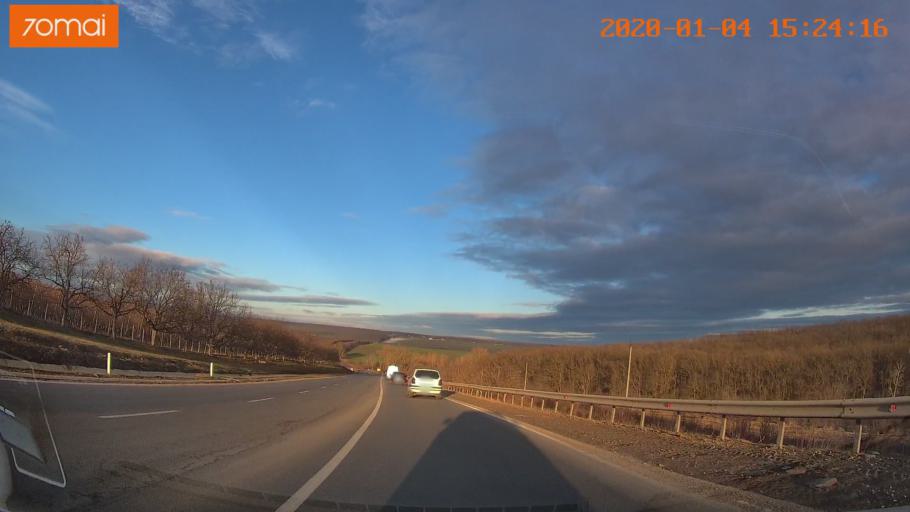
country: MD
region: Orhei
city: Orhei
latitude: 47.2746
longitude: 28.7956
